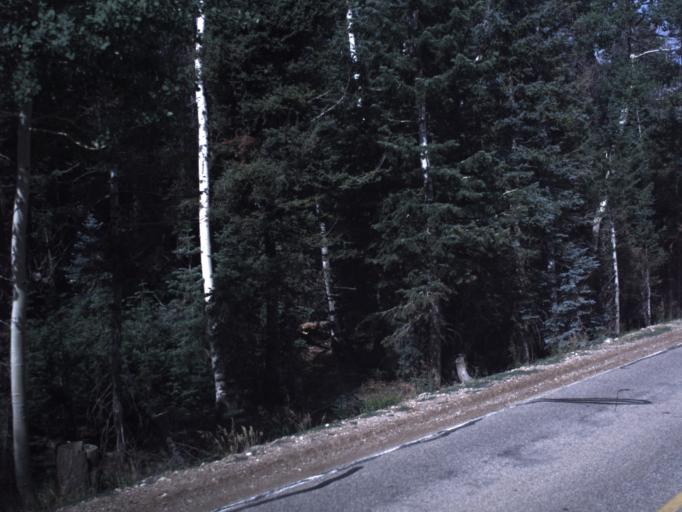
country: US
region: Utah
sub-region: Iron County
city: Parowan
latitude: 37.5193
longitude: -112.6494
